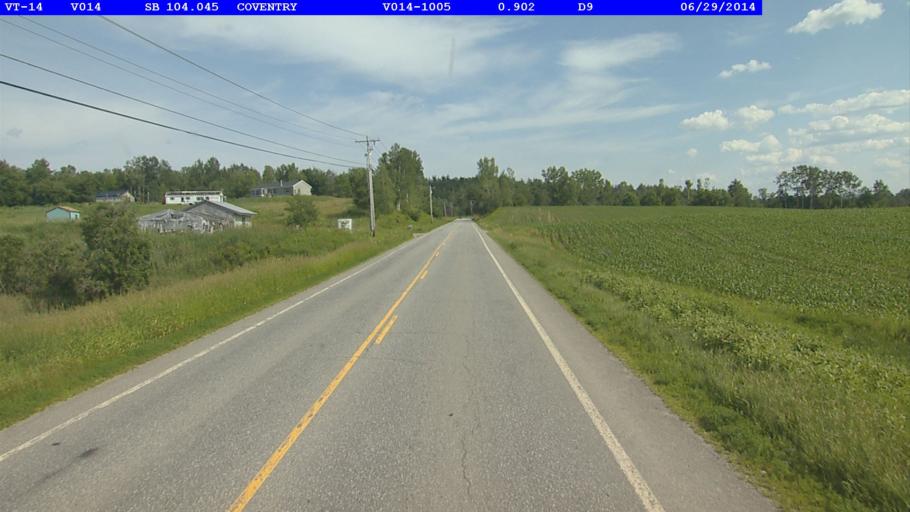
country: US
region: Vermont
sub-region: Orleans County
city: Newport
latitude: 44.8772
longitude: -72.2642
